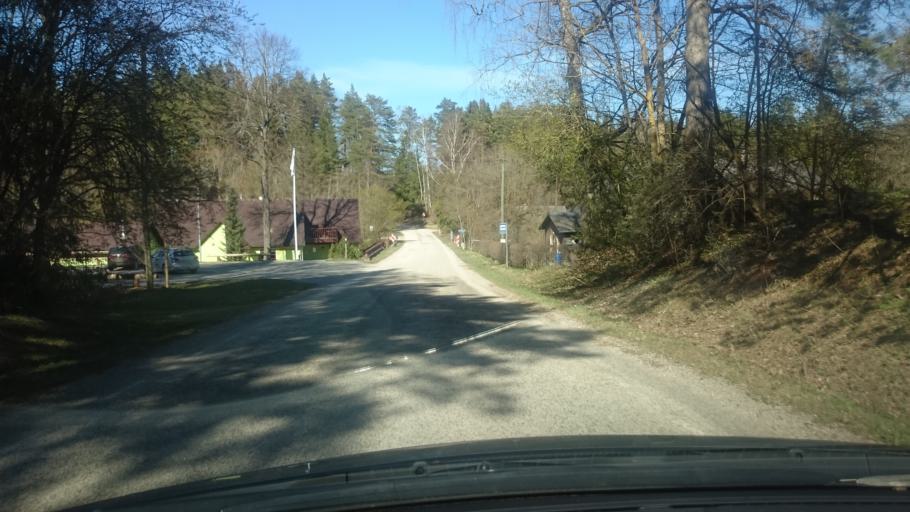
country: EE
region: Polvamaa
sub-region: Polva linn
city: Polva
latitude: 58.1388
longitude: 27.0186
